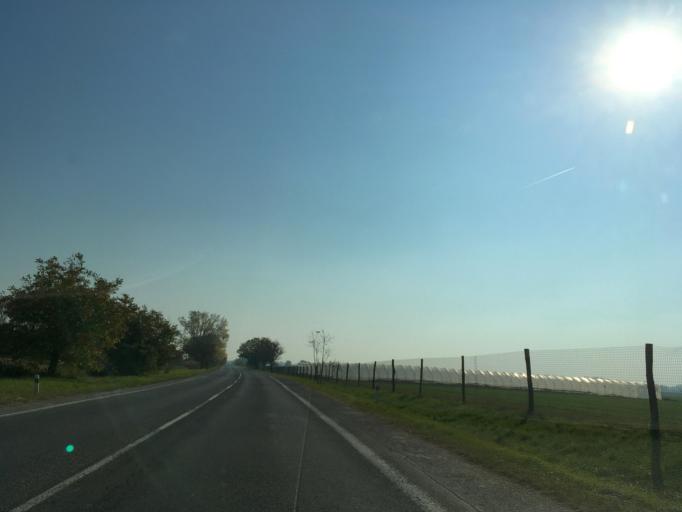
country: SK
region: Bratislavsky
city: Dunajska Luzna
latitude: 48.0578
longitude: 17.2843
